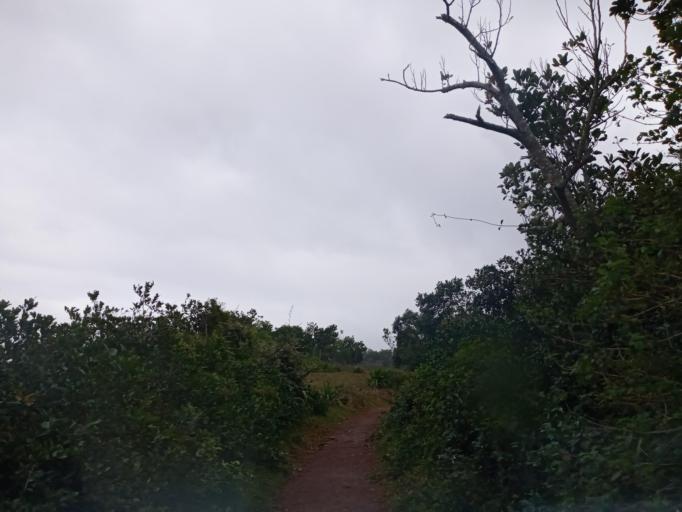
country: MG
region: Atsimo-Atsinanana
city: Vohipaho
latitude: -23.8290
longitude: 47.5420
